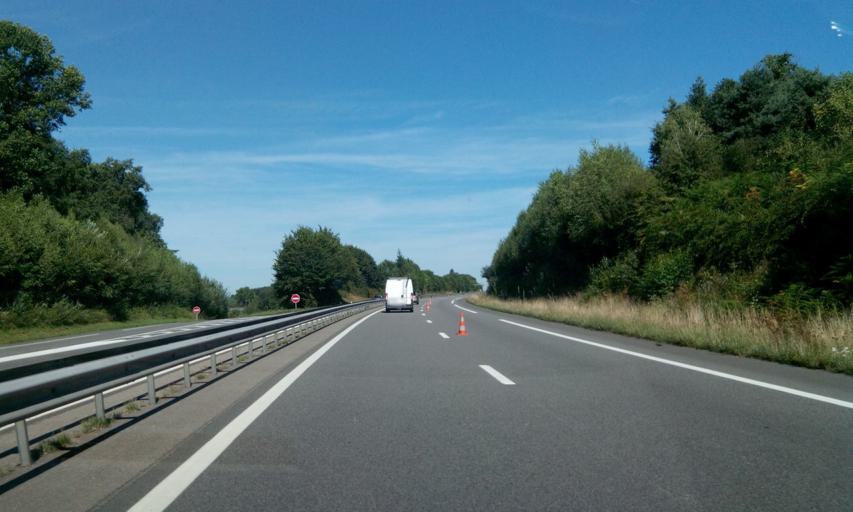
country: FR
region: Limousin
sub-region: Departement de la Haute-Vienne
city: Saint-Victurnien
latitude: 45.8927
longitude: 1.0379
